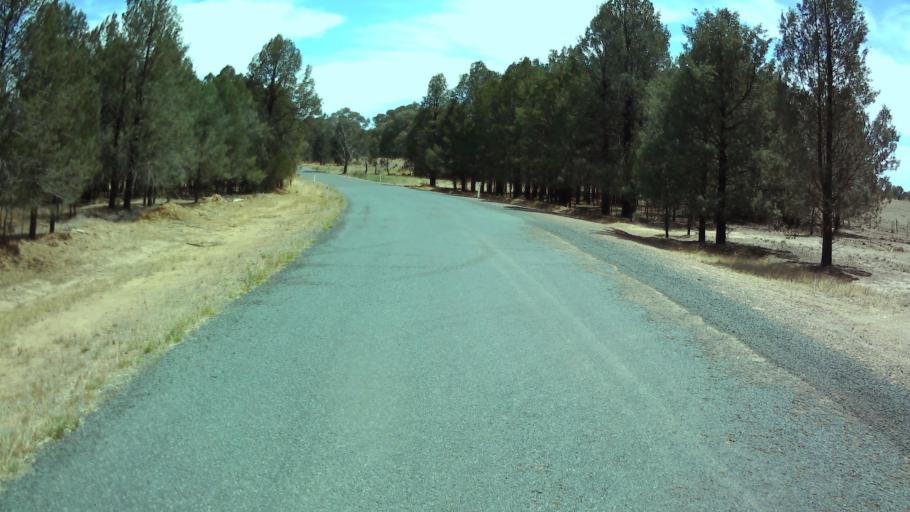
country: AU
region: New South Wales
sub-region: Weddin
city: Grenfell
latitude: -33.7722
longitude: 148.2064
